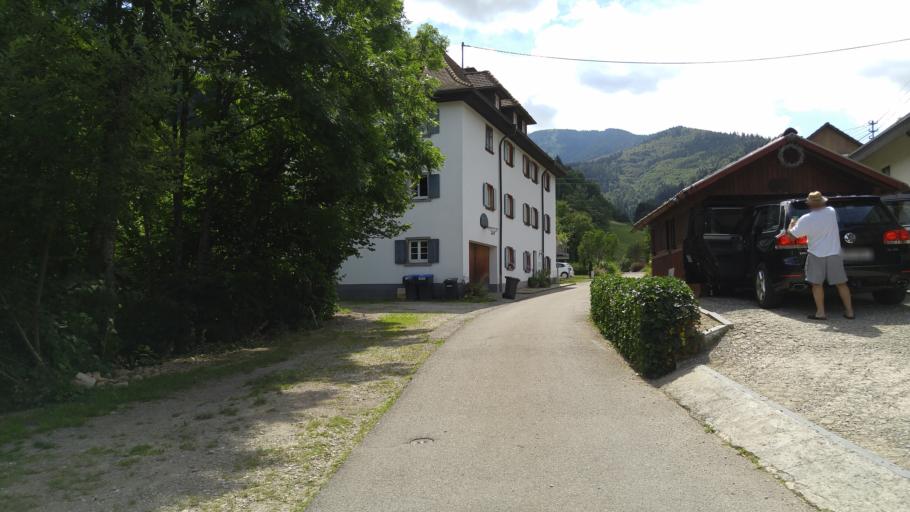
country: DE
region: Baden-Wuerttemberg
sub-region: Freiburg Region
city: Muenstertal/Schwarzwald
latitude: 47.8484
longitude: 7.7917
